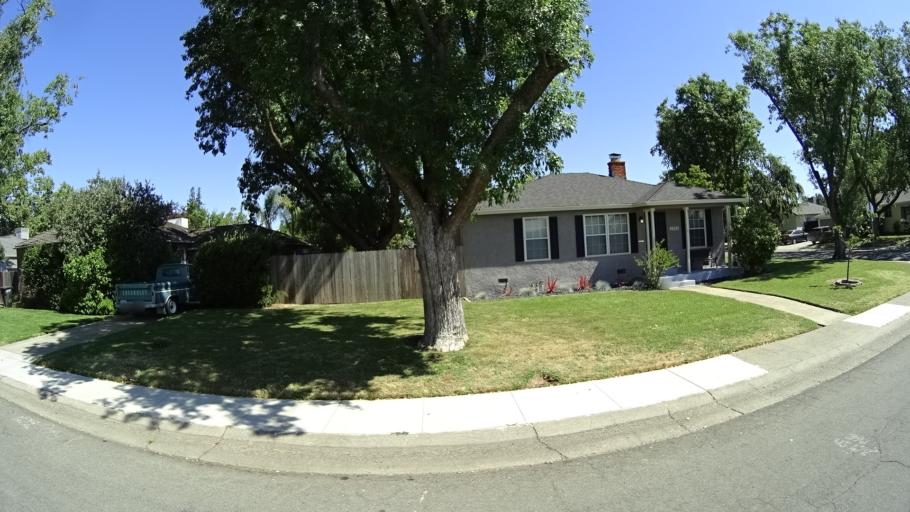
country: US
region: California
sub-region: Sacramento County
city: Parkway
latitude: 38.5257
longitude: -121.4897
